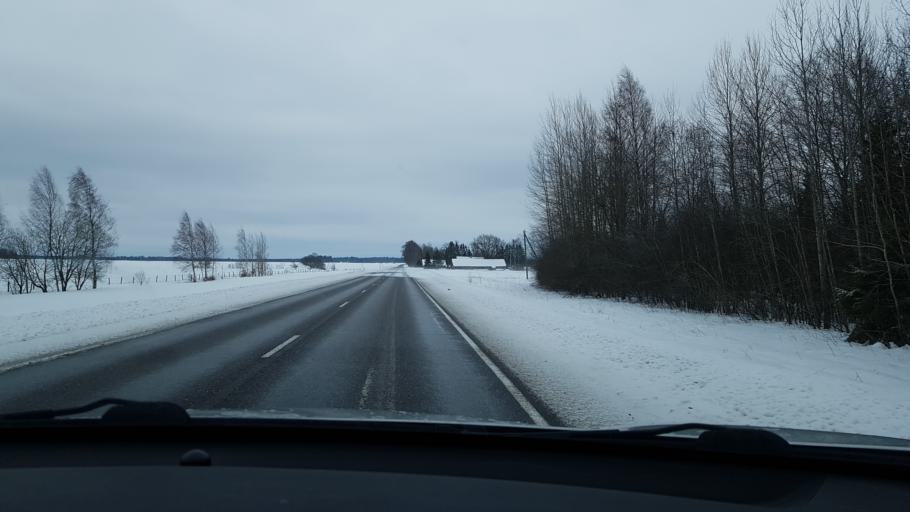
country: EE
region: Jaervamaa
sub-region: Jaerva-Jaani vald
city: Jarva-Jaani
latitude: 59.1258
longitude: 25.7839
